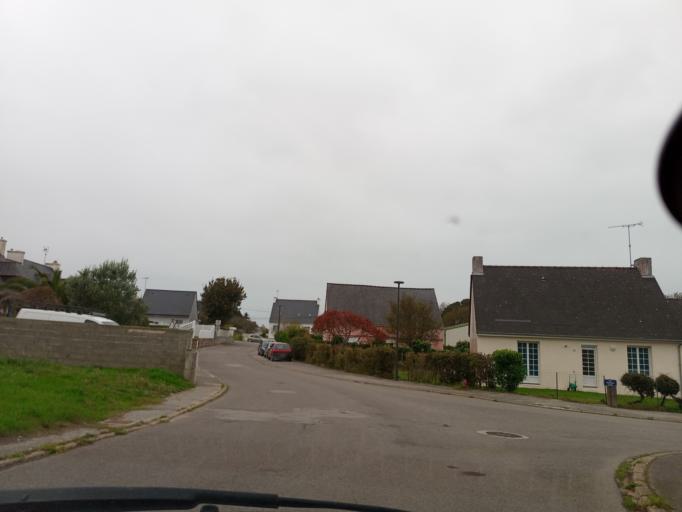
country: FR
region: Brittany
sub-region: Departement du Finistere
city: Esquibien
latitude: 48.0291
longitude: -4.5485
